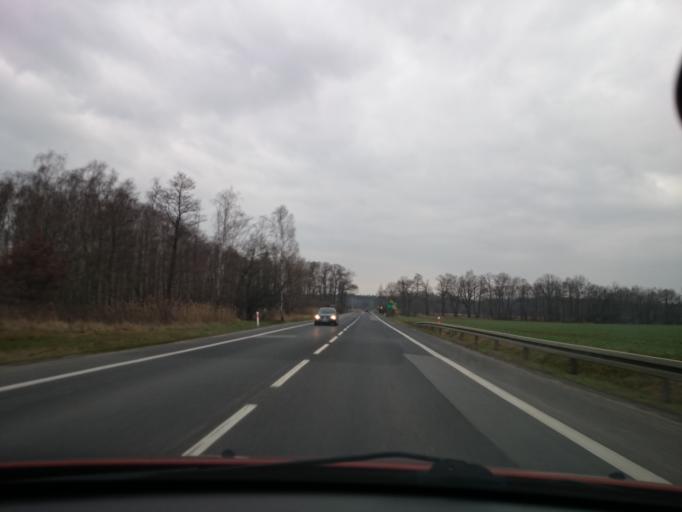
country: PL
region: Opole Voivodeship
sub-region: Powiat opolski
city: Dabrowa
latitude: 50.6584
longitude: 17.6906
